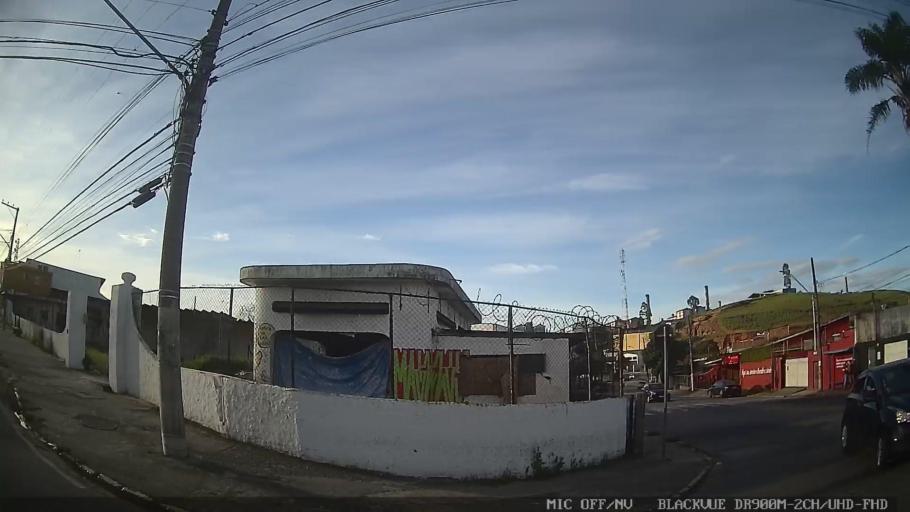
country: BR
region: Sao Paulo
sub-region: Mogi das Cruzes
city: Mogi das Cruzes
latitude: -23.5112
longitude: -46.1433
